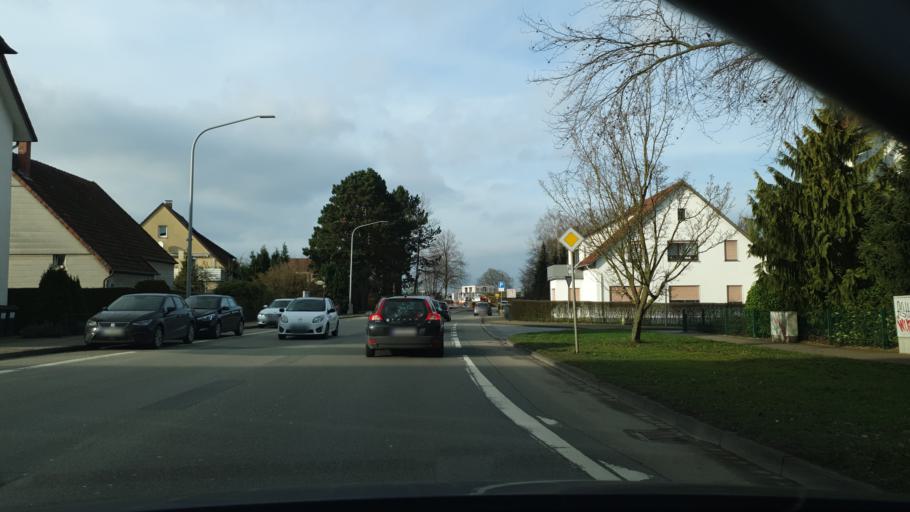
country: DE
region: North Rhine-Westphalia
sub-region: Regierungsbezirk Detmold
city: Bielefeld
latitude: 52.0728
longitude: 8.5154
